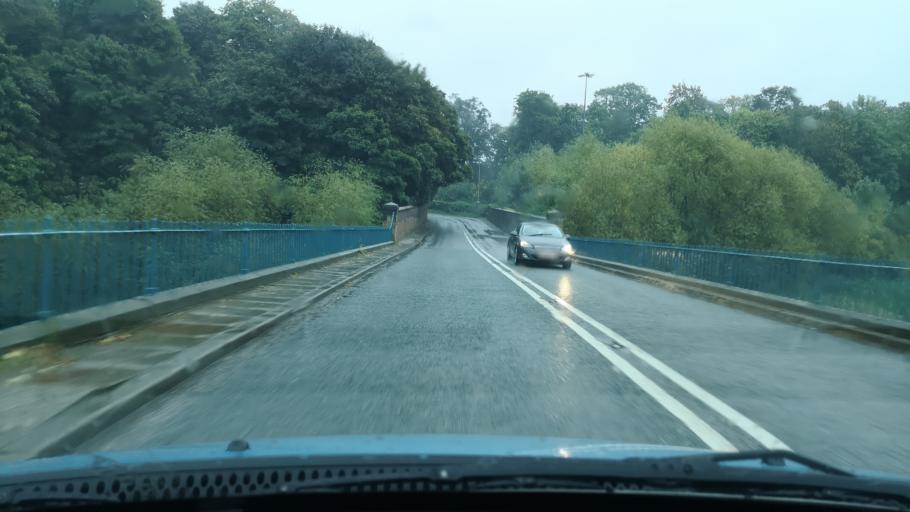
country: GB
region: England
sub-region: City and Borough of Wakefield
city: Fitzwilliam
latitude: 53.6519
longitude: -1.3928
